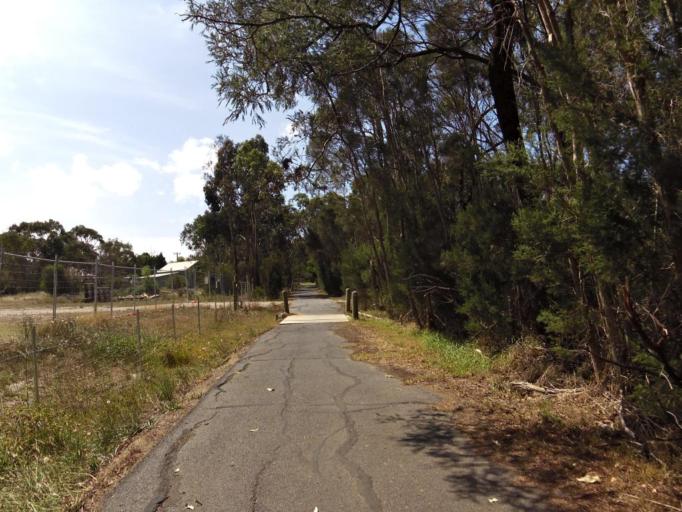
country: AU
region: Victoria
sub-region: Mornington Peninsula
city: Crib Point
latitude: -38.3522
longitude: 145.1664
